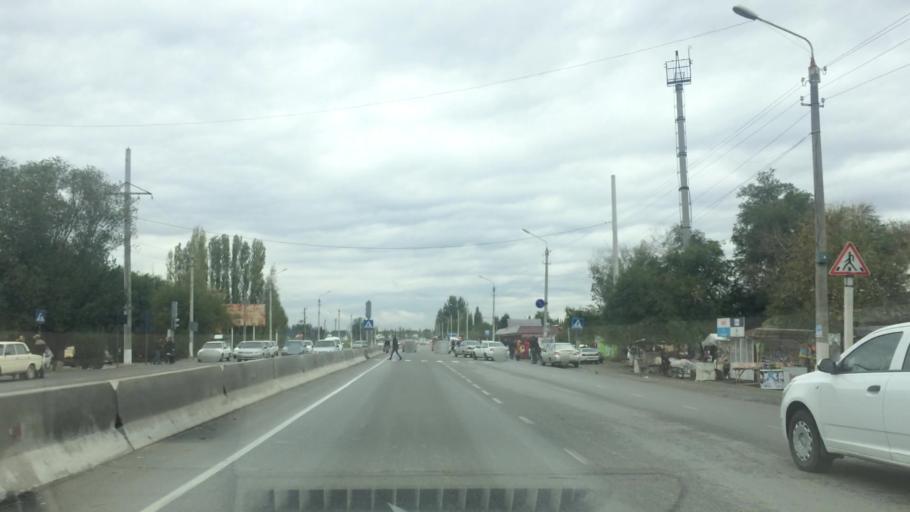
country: UZ
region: Jizzax
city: Jizzax
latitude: 39.9833
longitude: 67.5728
